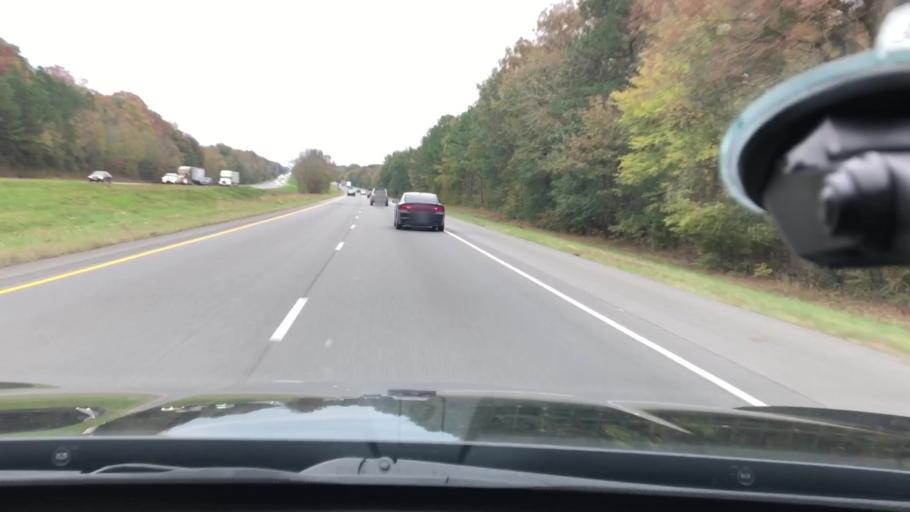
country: US
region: Arkansas
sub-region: Hempstead County
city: Hope
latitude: 33.6306
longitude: -93.7248
